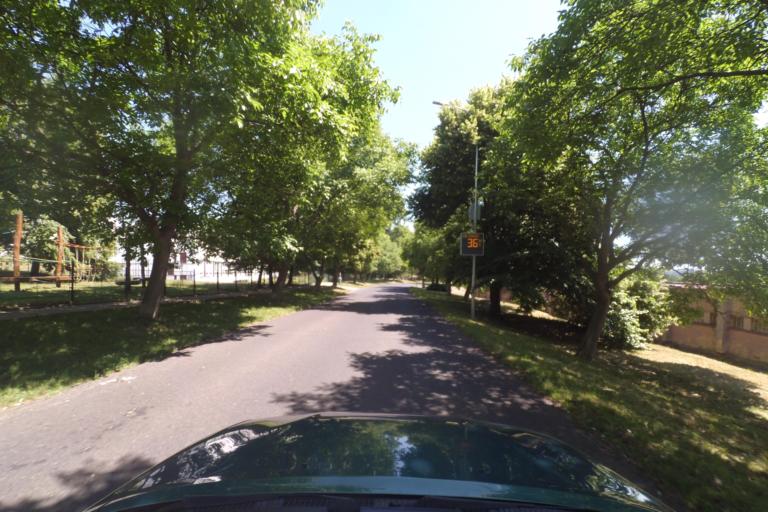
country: CZ
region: Ustecky
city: Chlumec
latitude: 50.6977
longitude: 13.9357
